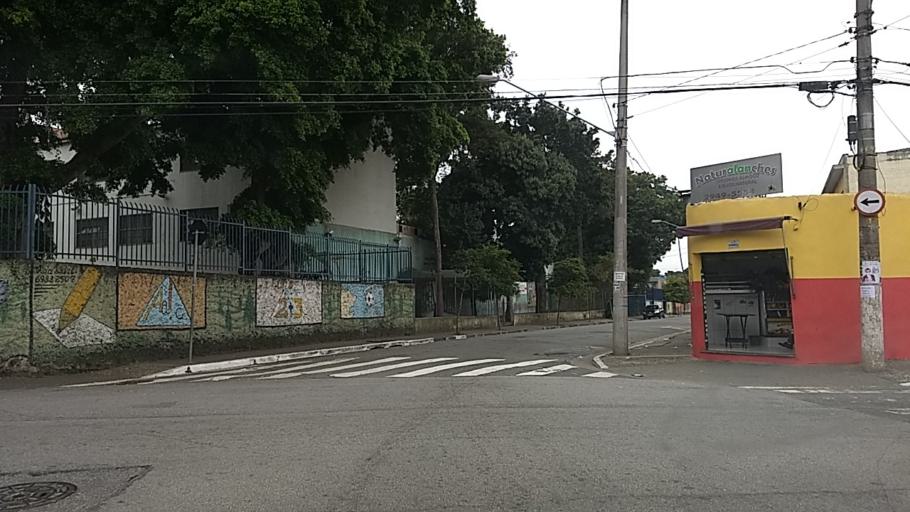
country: BR
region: Sao Paulo
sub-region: Guarulhos
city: Guarulhos
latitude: -23.4929
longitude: -46.5740
